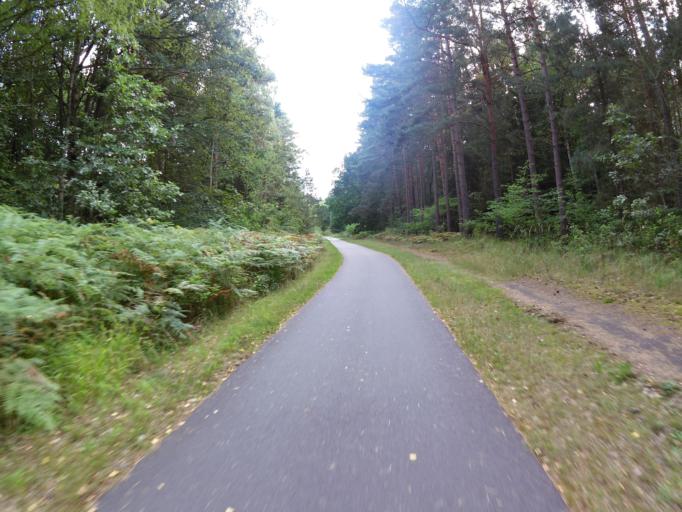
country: DE
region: Mecklenburg-Vorpommern
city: Karlshagen
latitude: 54.1356
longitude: 13.8163
